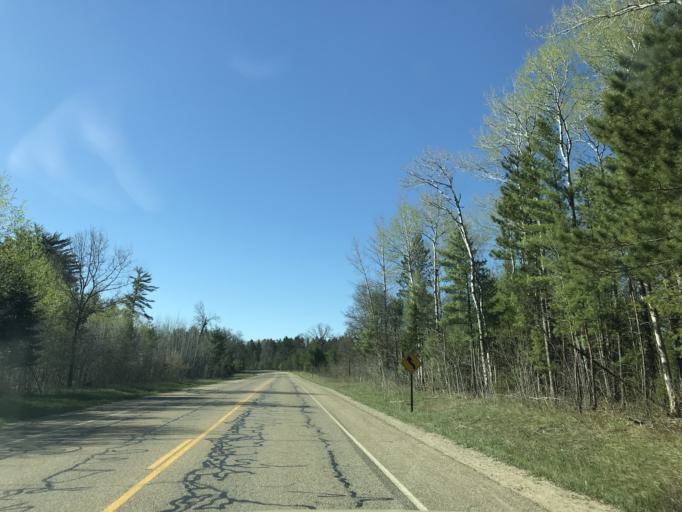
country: US
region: Michigan
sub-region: Crawford County
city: Grayling
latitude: 44.7180
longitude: -84.7445
